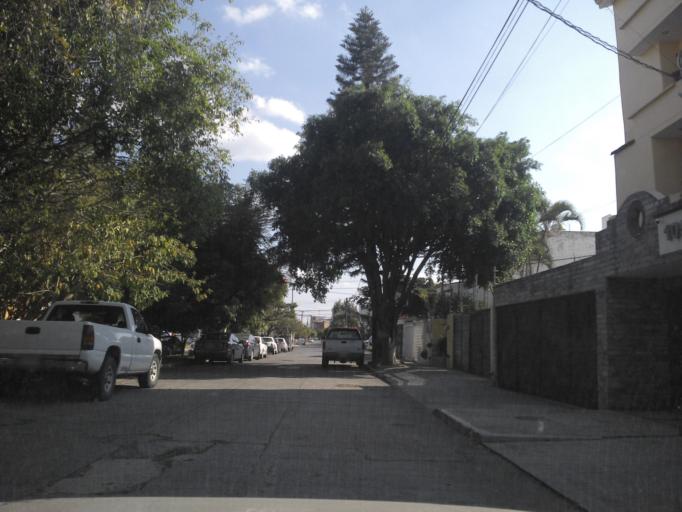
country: MX
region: Jalisco
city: Guadalajara
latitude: 20.6597
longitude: -103.4142
